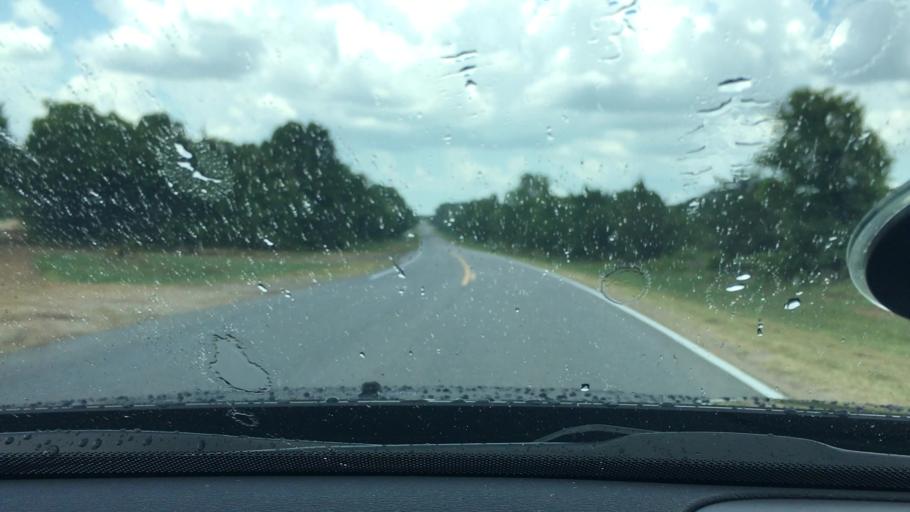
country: US
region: Oklahoma
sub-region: Johnston County
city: Tishomingo
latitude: 34.2112
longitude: -96.7059
